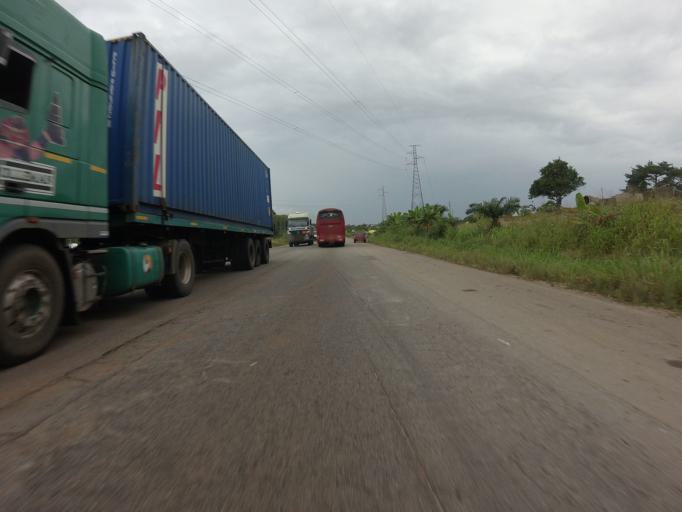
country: GH
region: Ashanti
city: Konongo
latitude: 6.6166
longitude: -1.1714
